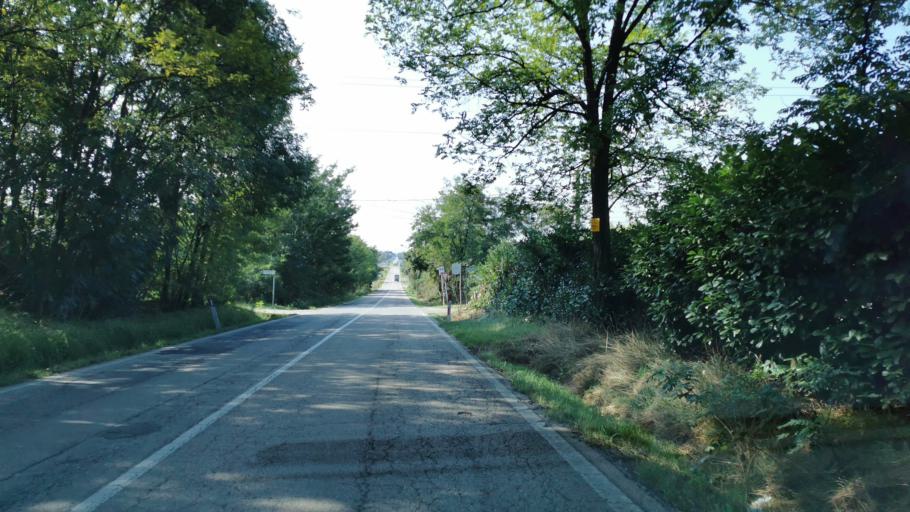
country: IT
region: Piedmont
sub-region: Provincia di Torino
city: Lombardore
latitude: 45.2083
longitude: 7.7289
